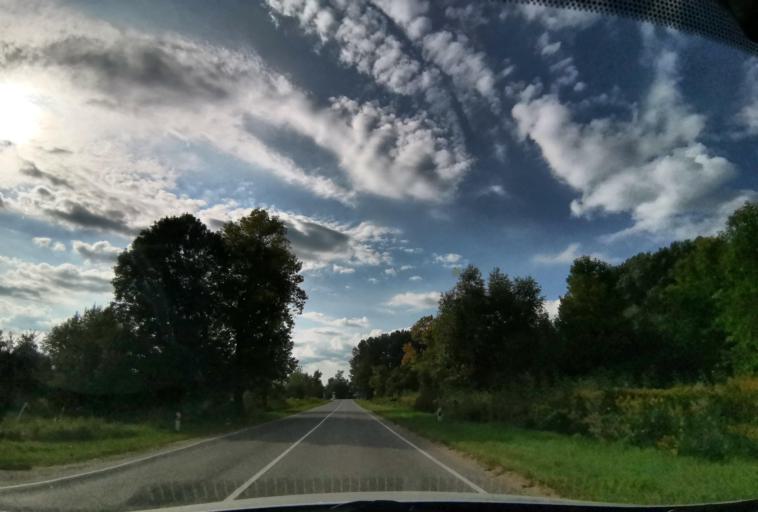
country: RU
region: Kaliningrad
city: Neman
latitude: 55.0203
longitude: 22.0787
